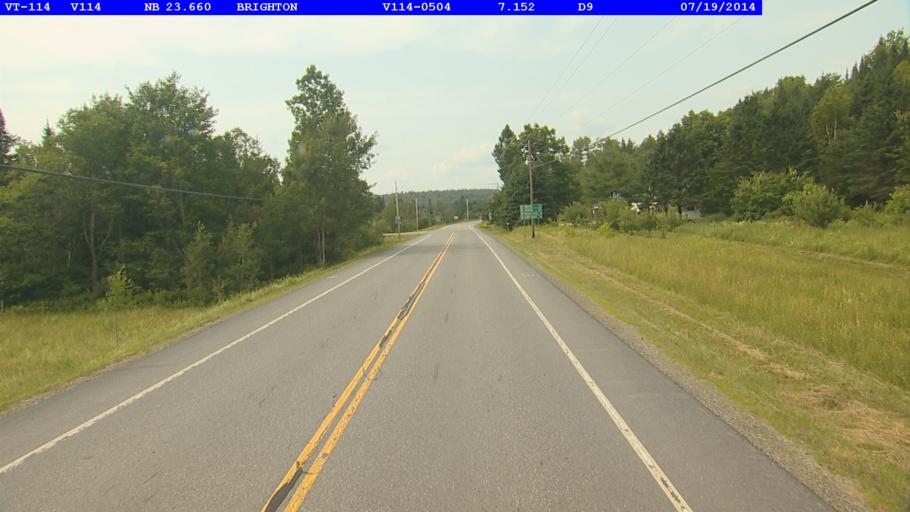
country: CA
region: Quebec
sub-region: Estrie
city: Coaticook
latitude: 44.8437
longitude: -71.9088
